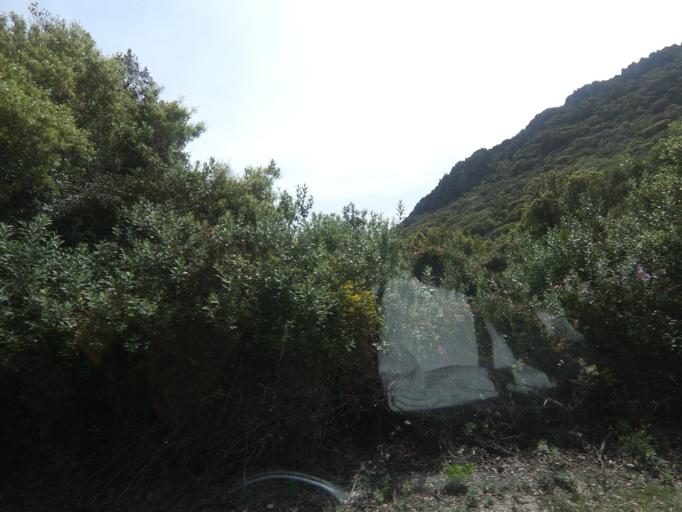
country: PT
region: Setubal
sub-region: Sesimbra
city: Sesimbra
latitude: 38.4705
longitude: -9.0017
